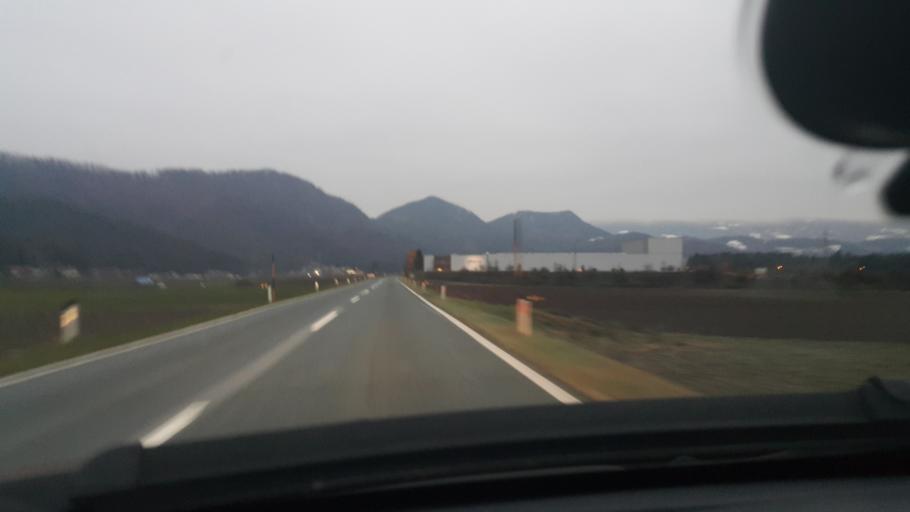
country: AT
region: Carinthia
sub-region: Politischer Bezirk Volkermarkt
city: Ruden
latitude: 46.6539
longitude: 14.8151
